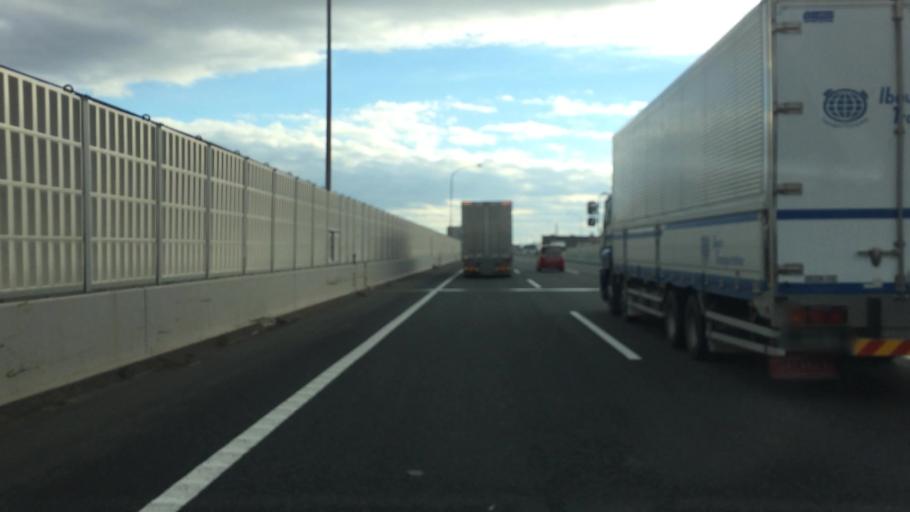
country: JP
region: Chiba
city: Funabashi
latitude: 35.6896
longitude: 139.9742
